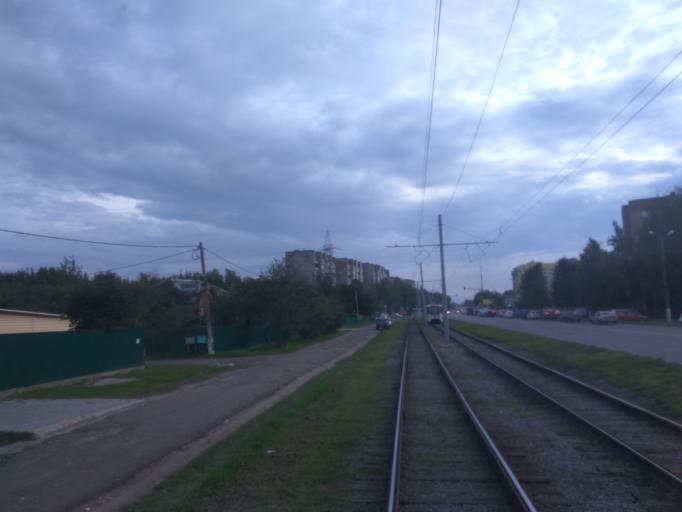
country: RU
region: Moskovskaya
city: Kolomna
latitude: 55.0790
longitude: 38.7622
